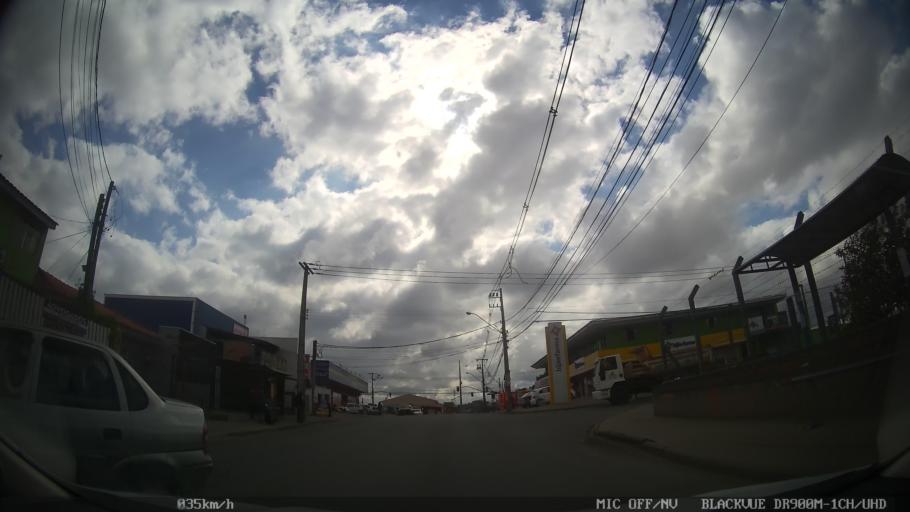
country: BR
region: Parana
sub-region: Pinhais
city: Pinhais
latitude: -25.3727
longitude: -49.2002
